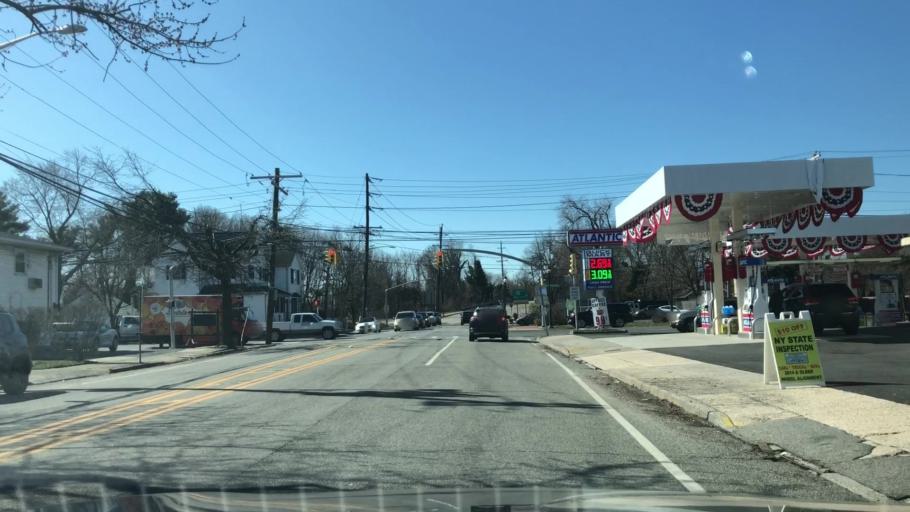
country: US
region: New York
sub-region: Nassau County
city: North Valley Stream
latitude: 40.6855
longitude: -73.6878
